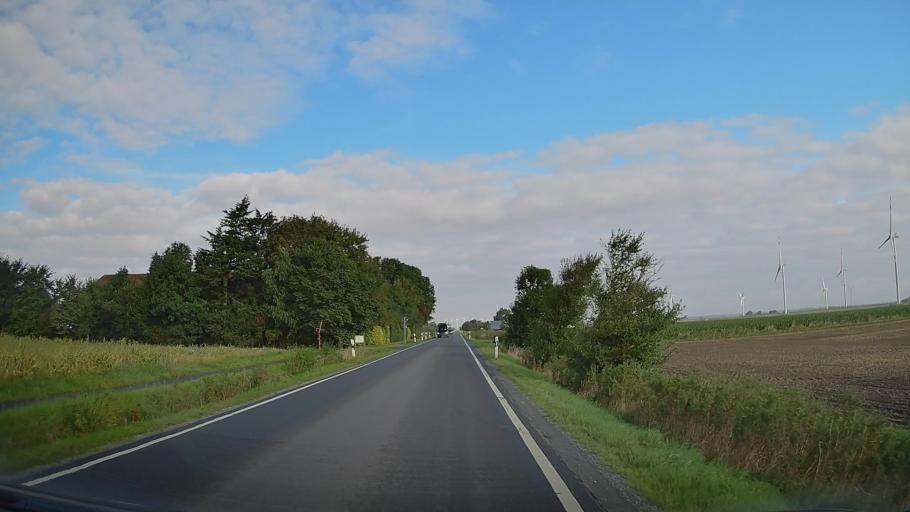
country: DE
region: Schleswig-Holstein
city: Reussenkoge
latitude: 54.5718
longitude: 8.9287
